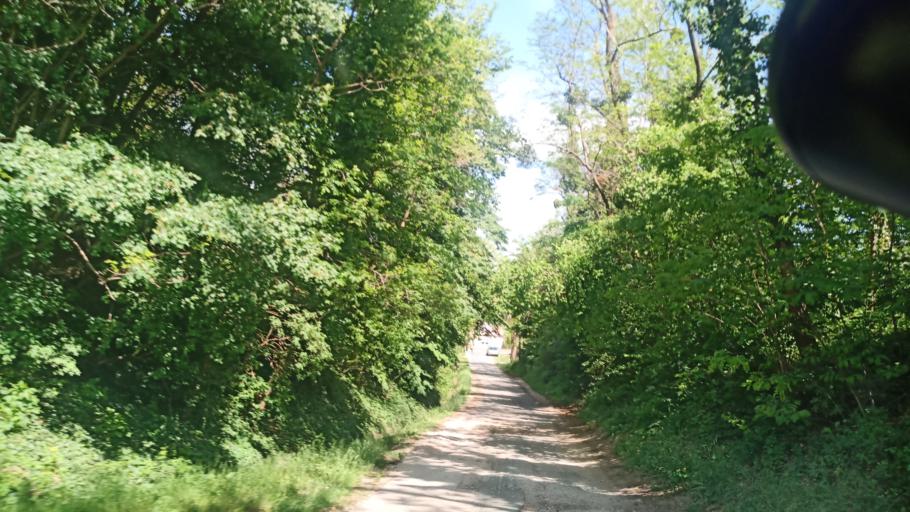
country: HU
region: Zala
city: Zalakomar
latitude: 46.6171
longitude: 17.1143
